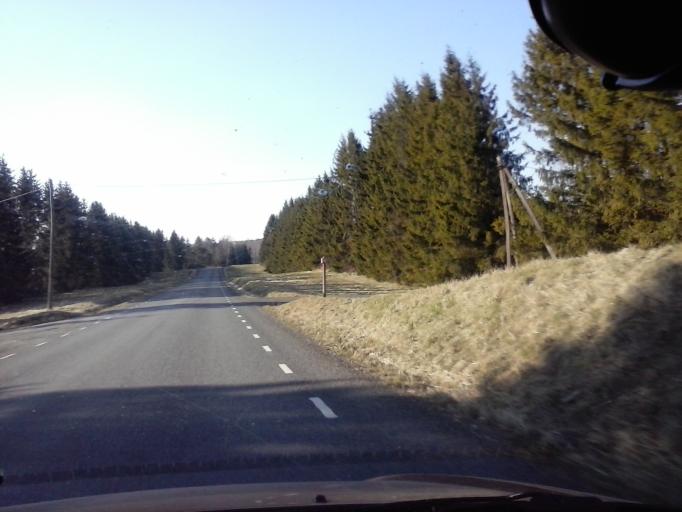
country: EE
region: Tartu
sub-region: UElenurme vald
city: Ulenurme
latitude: 58.1691
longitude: 26.8379
